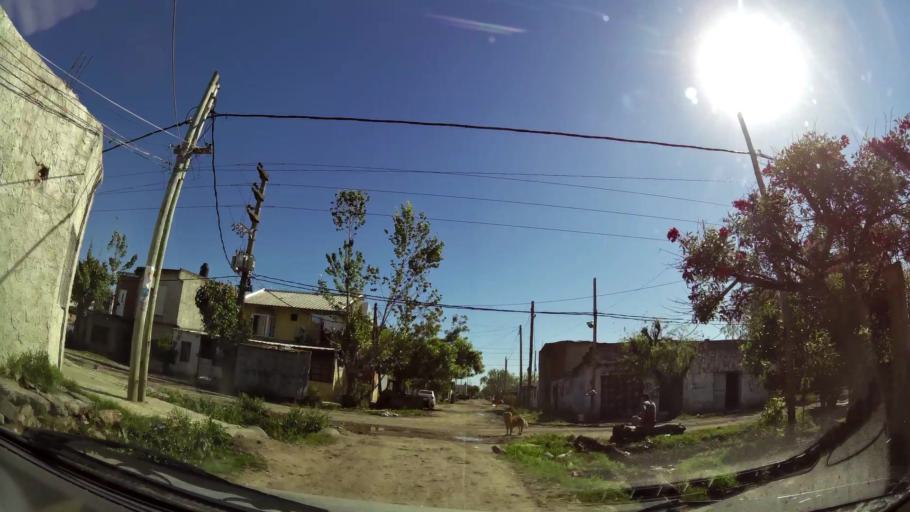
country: AR
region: Buenos Aires
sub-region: Partido de Quilmes
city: Quilmes
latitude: -34.7630
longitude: -58.3113
